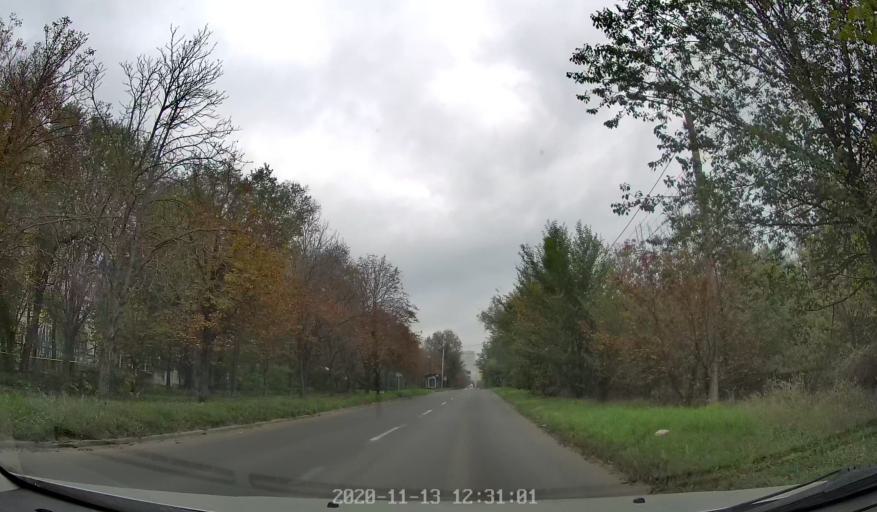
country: MD
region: Chisinau
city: Chisinau
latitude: 46.9750
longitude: 28.8355
